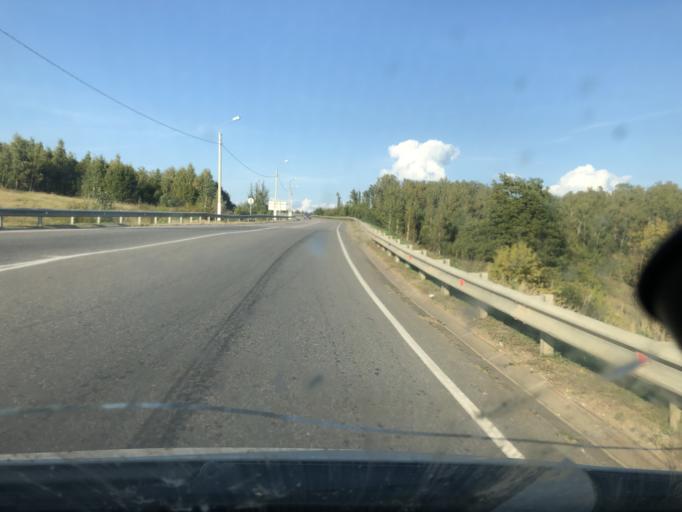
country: RU
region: Kaluga
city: Kozel'sk
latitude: 54.0602
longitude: 35.7894
